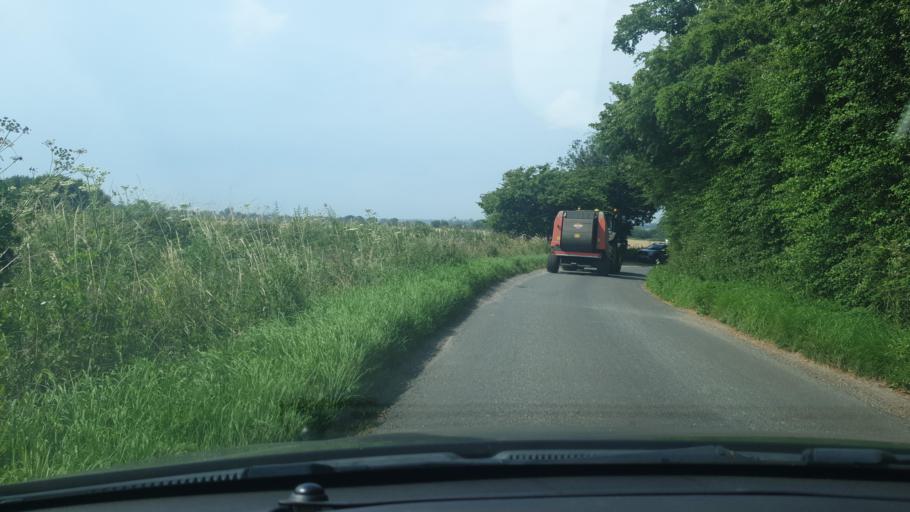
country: GB
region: England
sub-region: Suffolk
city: East Bergholt
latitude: 51.9488
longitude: 1.0123
